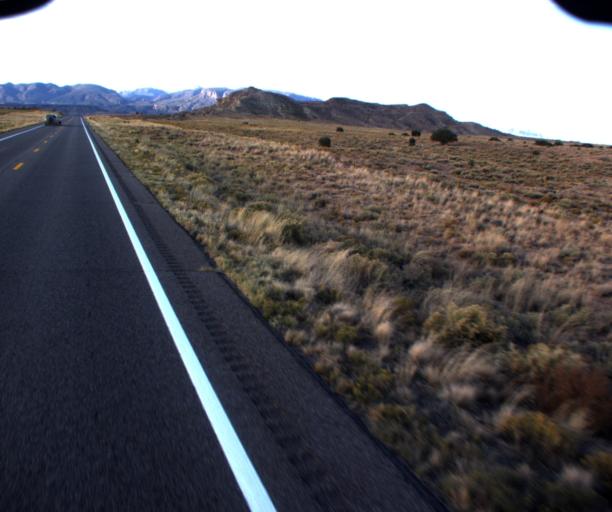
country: US
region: New Mexico
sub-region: San Juan County
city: Shiprock
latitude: 36.9525
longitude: -109.0703
